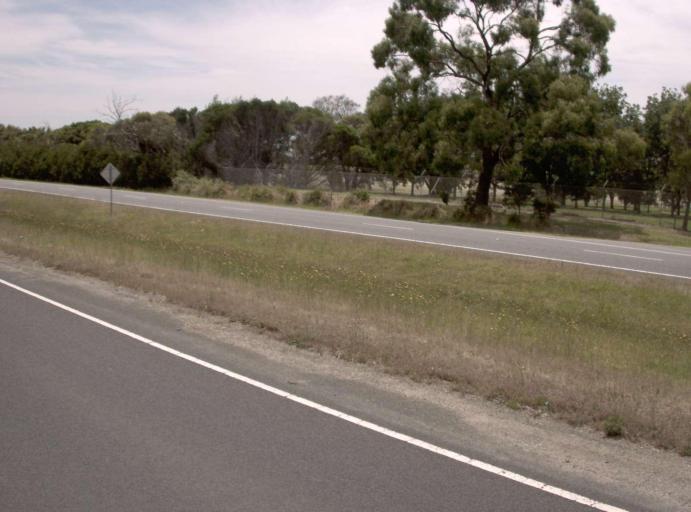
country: AU
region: Victoria
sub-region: Casey
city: Cranbourne South
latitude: -38.1204
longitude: 145.2307
